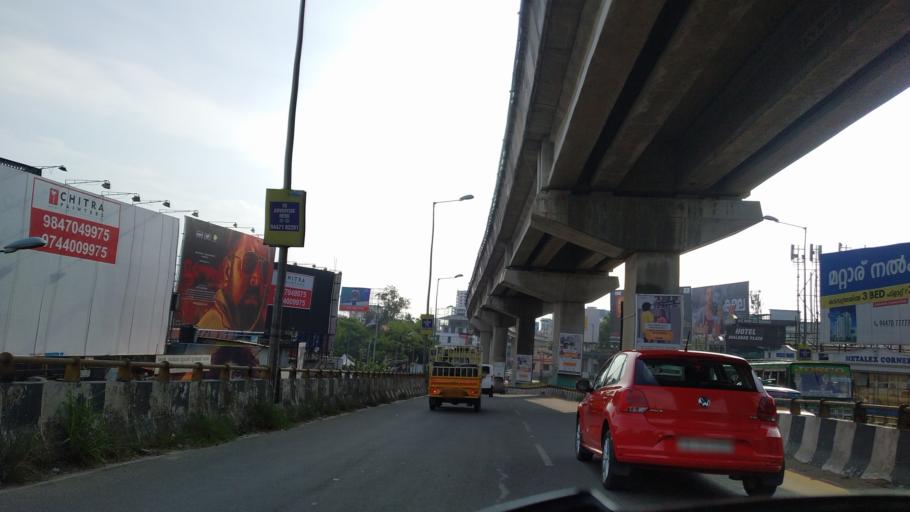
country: IN
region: Kerala
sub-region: Ernakulam
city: Cochin
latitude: 9.9894
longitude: 76.2868
